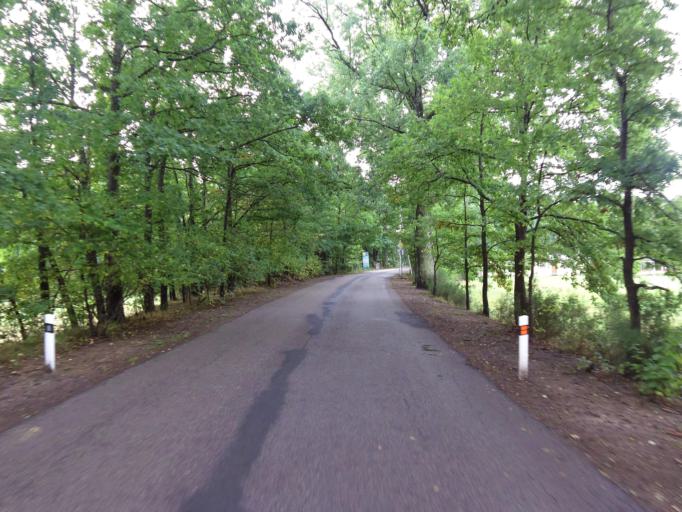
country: CZ
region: Jihocesky
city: Chlum u Trebone
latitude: 48.9756
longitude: 14.9545
